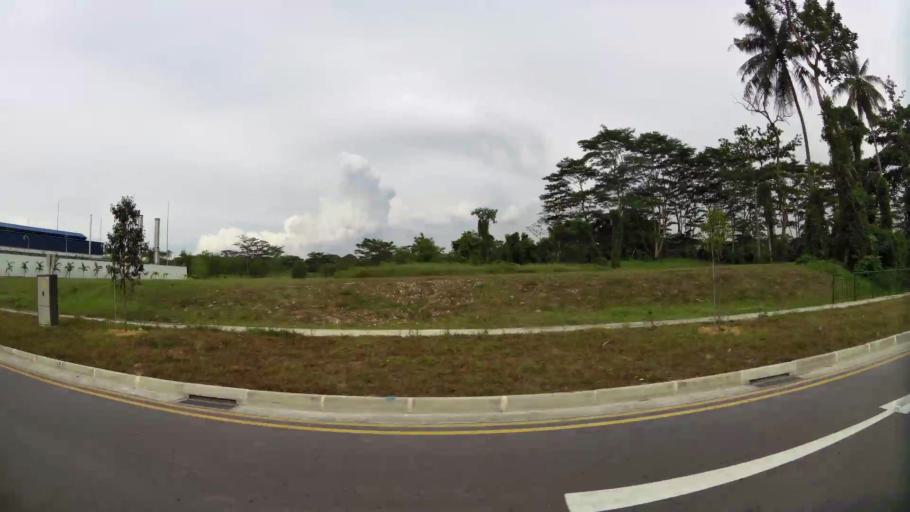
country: MY
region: Johor
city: Johor Bahru
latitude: 1.3580
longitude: 103.6947
